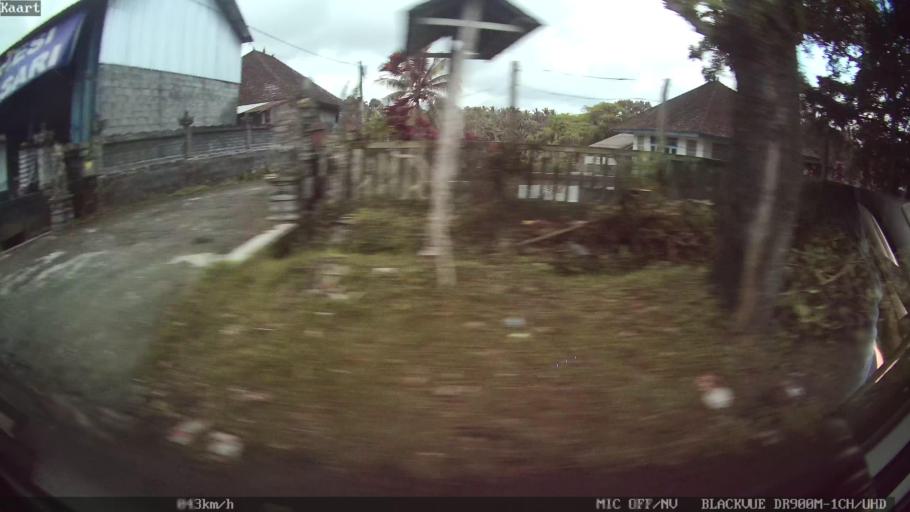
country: ID
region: Bali
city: Pohgending Kawan
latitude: -8.4383
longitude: 115.1424
